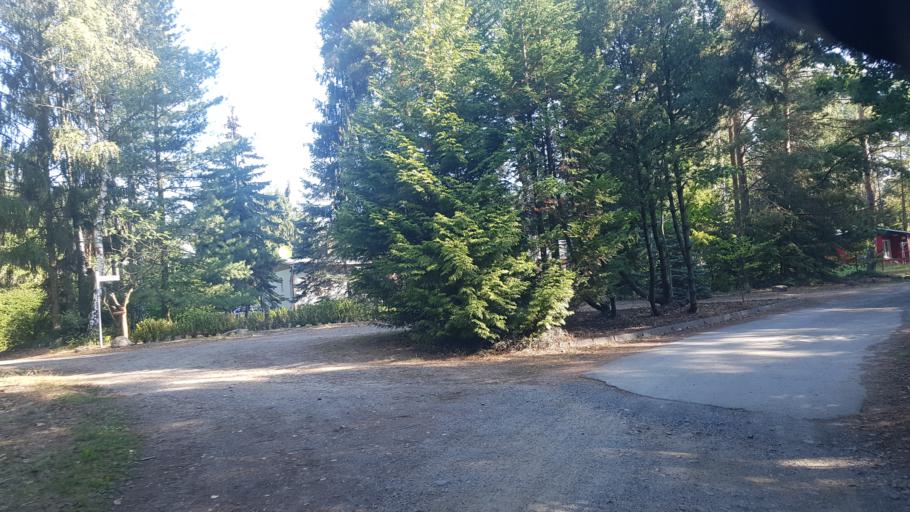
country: DE
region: Brandenburg
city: Plessa
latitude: 51.5128
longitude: 13.6505
